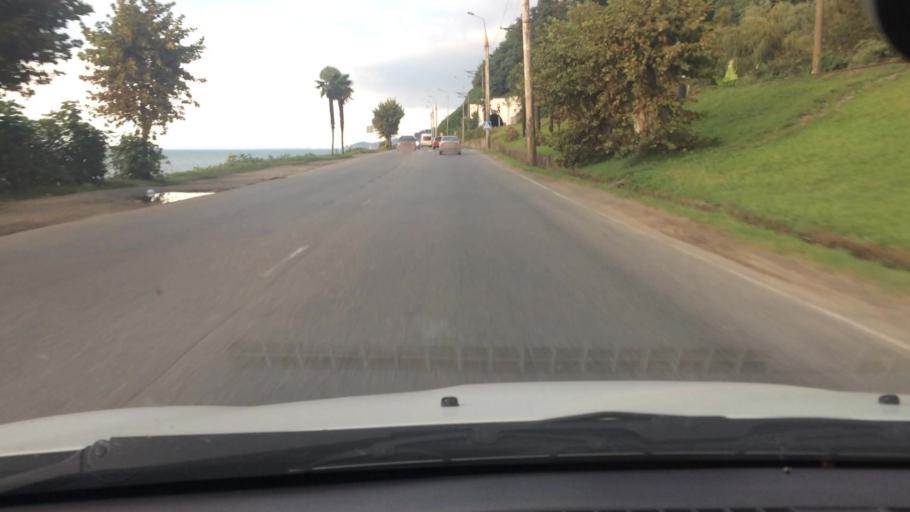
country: GE
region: Ajaria
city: Makhinjauri
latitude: 41.6686
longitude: 41.6870
